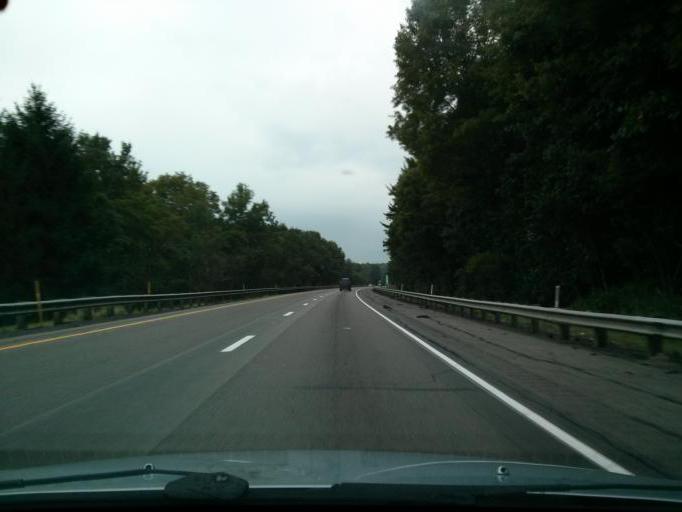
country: US
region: Pennsylvania
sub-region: Jefferson County
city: Brookville
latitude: 41.1579
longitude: -79.0016
